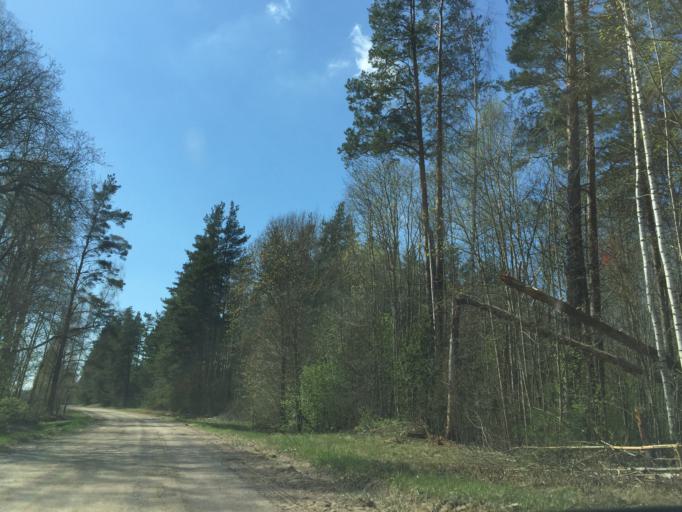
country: LV
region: Smiltene
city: Smiltene
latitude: 57.5673
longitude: 25.9128
